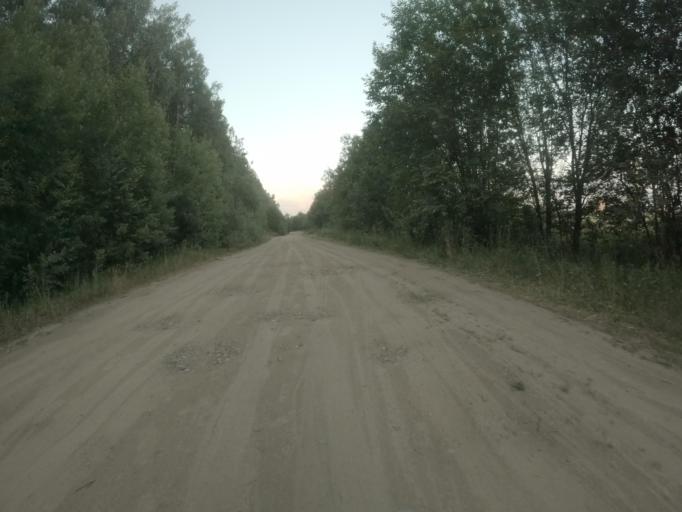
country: RU
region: Leningrad
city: Yanino Vtoroye
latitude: 59.9589
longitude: 30.5572
